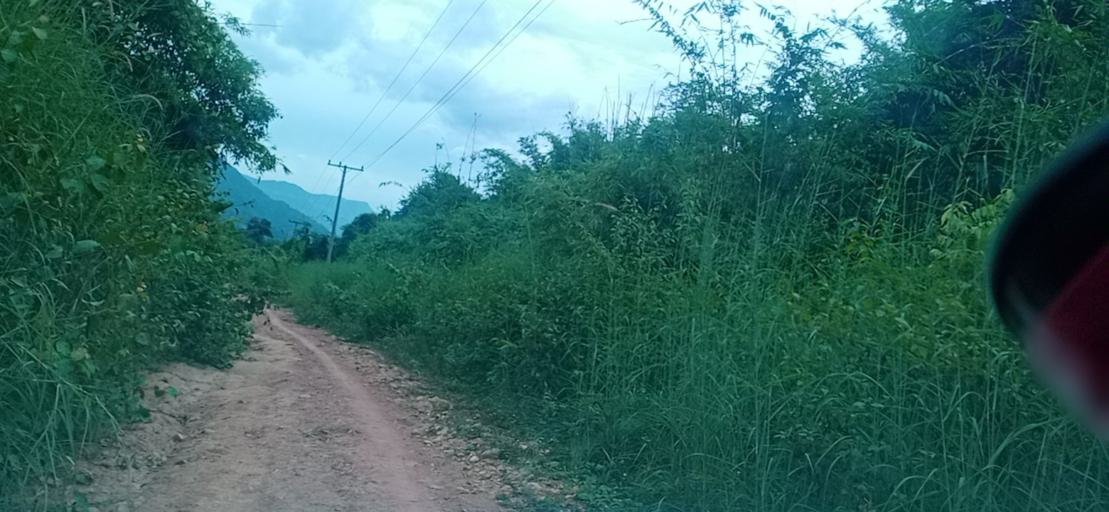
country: TH
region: Changwat Bueng Kan
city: Pak Khat
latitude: 18.5629
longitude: 103.2758
